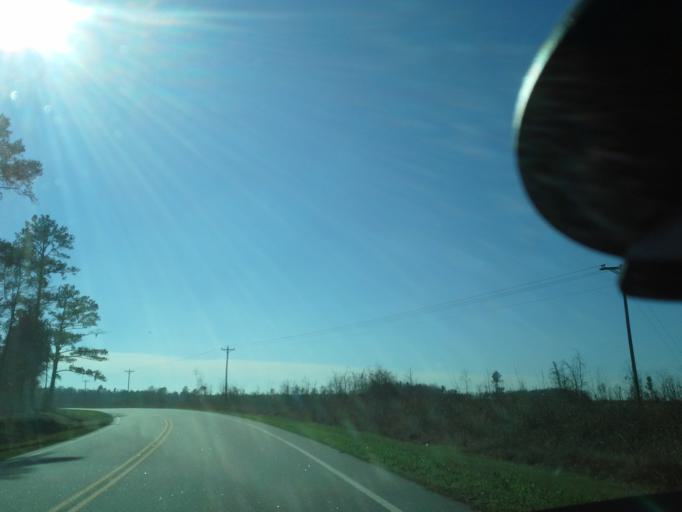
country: US
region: North Carolina
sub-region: Beaufort County
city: Belhaven
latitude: 35.5680
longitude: -76.6962
